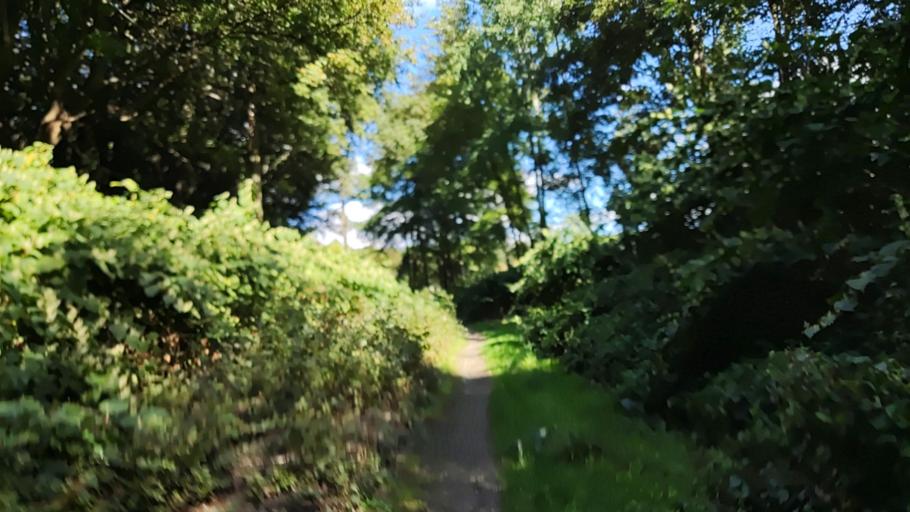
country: DE
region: North Rhine-Westphalia
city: Witten
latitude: 51.4575
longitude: 7.3163
